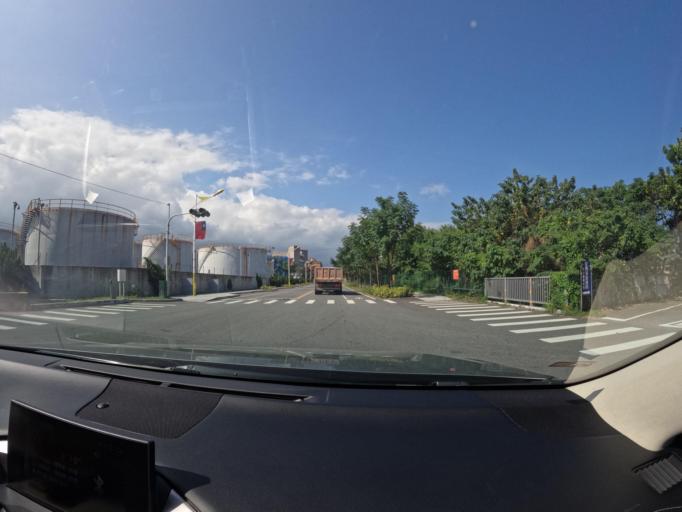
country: TW
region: Taiwan
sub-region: Hualien
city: Hualian
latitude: 23.9974
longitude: 121.6332
